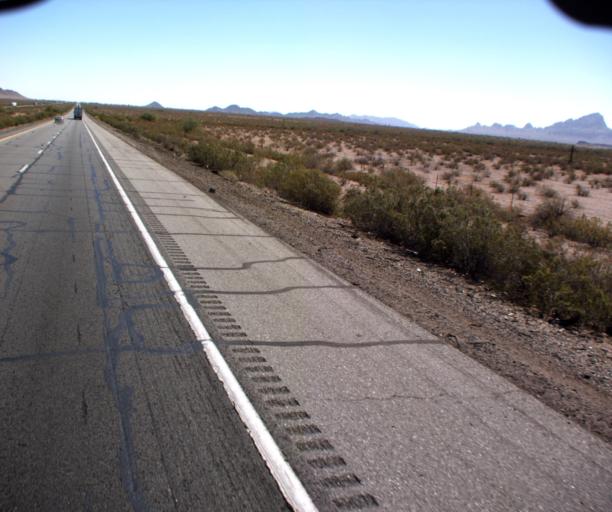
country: US
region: Arizona
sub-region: Maricopa County
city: Buckeye
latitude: 33.5265
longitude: -113.1066
